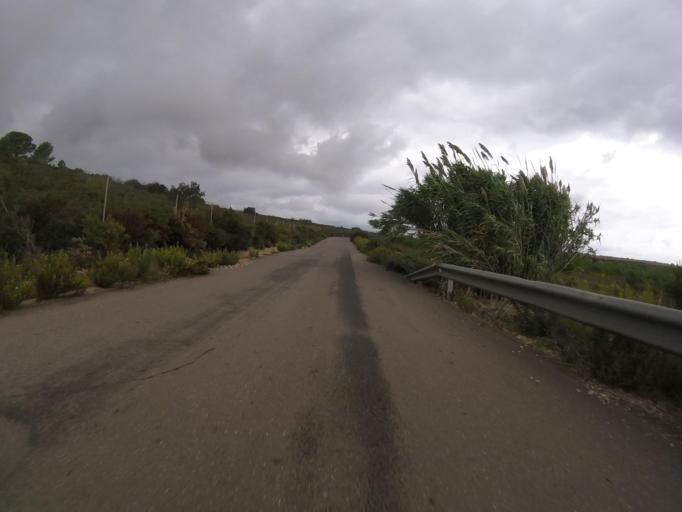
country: ES
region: Valencia
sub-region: Provincia de Castello
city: Benlloch
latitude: 40.2160
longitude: 0.0861
